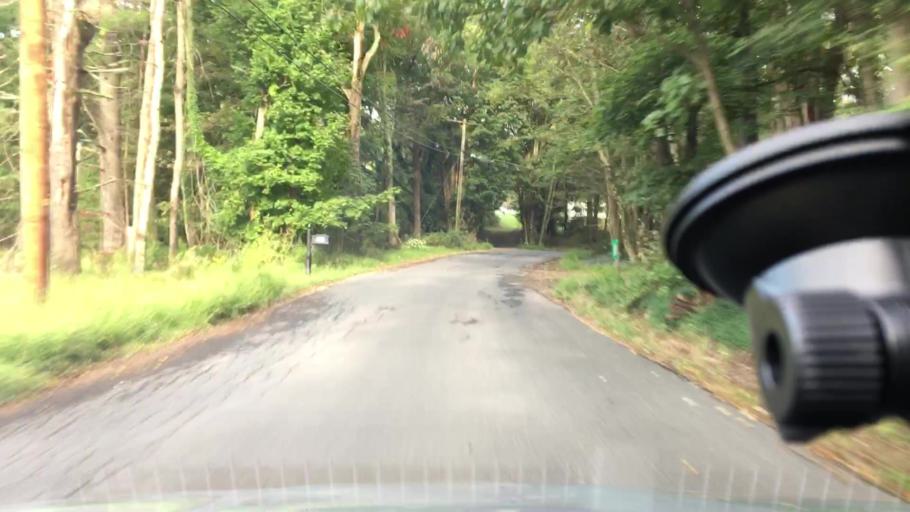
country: US
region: Pennsylvania
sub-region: Monroe County
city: Mountainhome
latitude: 41.1625
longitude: -75.2651
